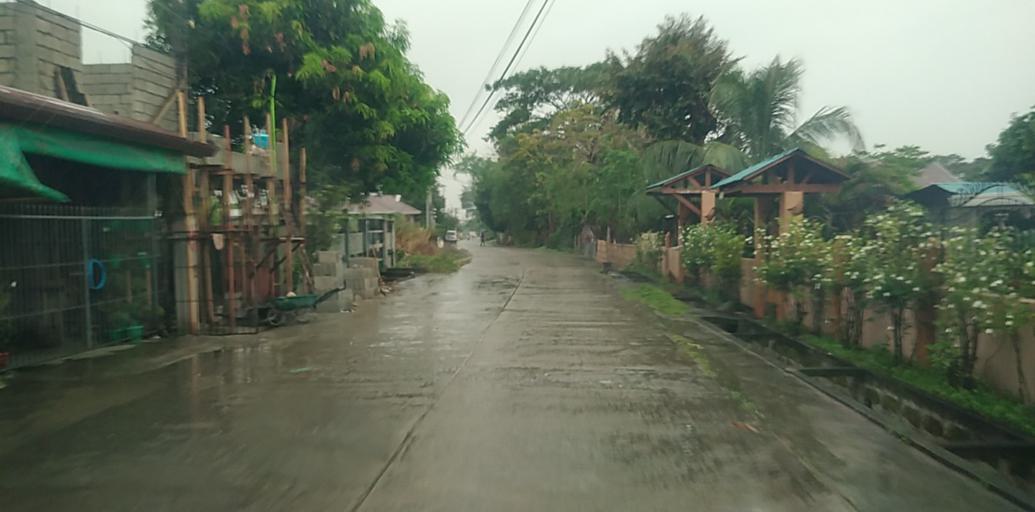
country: PH
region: Central Luzon
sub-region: Province of Pampanga
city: Arenas
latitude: 15.1737
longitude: 120.6828
